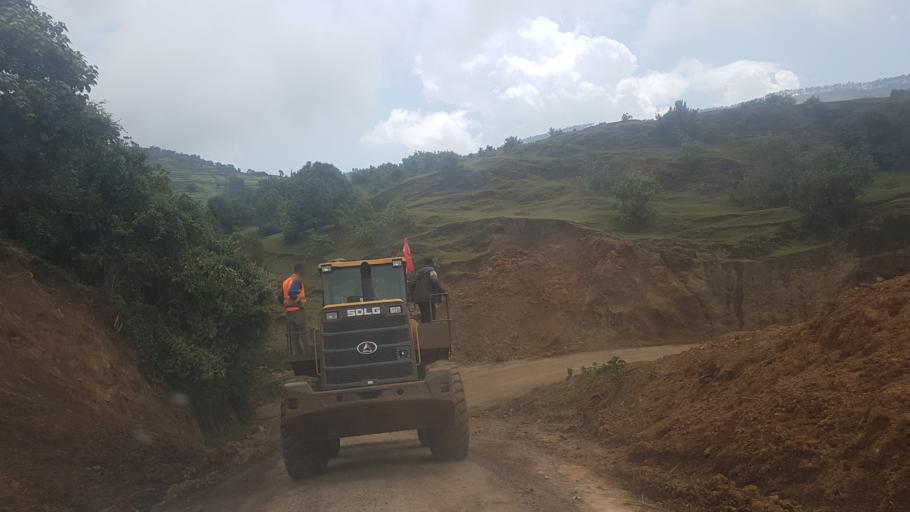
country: ET
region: Southern Nations, Nationalities, and People's Region
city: Arba Minch'
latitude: 6.3228
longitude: 37.5392
